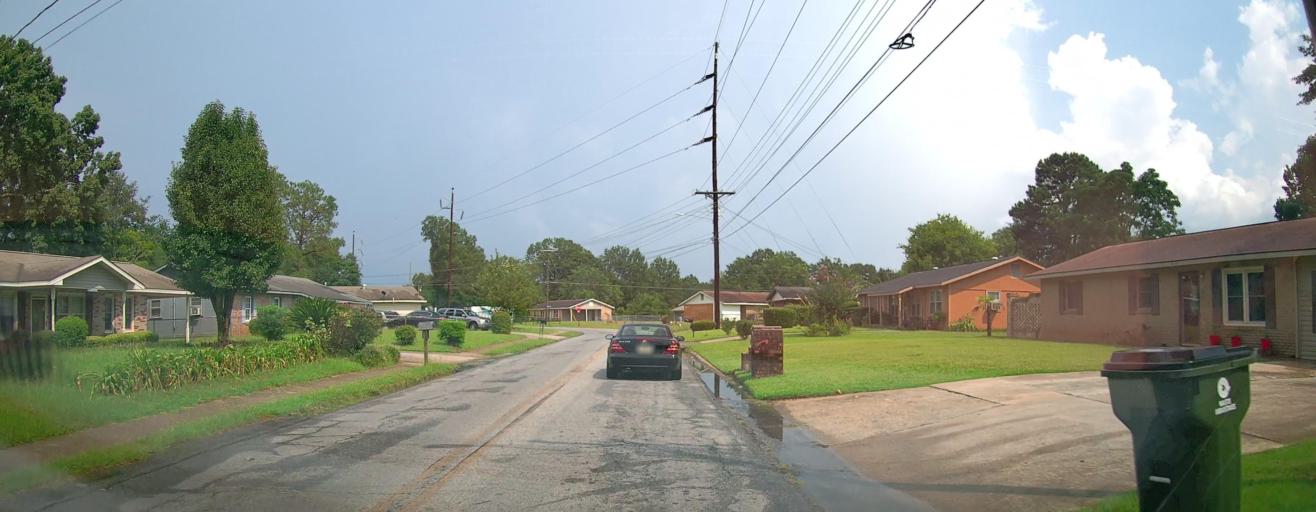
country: US
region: Georgia
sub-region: Houston County
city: Warner Robins
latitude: 32.6498
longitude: -83.6238
